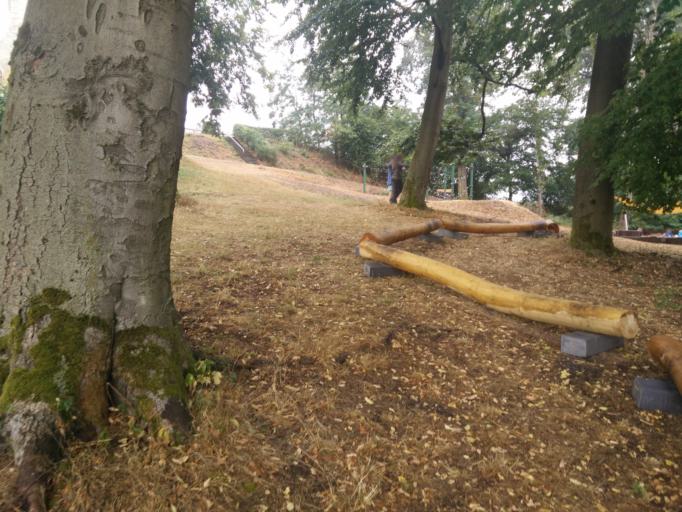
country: DE
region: Thuringia
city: Immelborn
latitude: 50.8161
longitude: 10.2640
